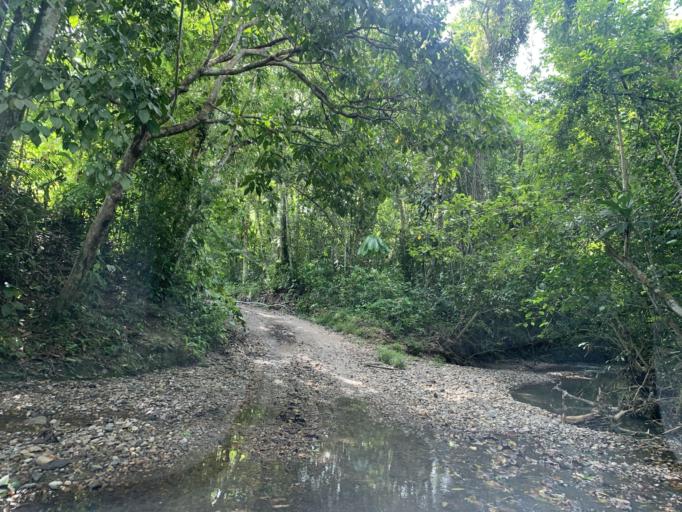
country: CO
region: Boyaca
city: Puerto Boyaca
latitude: 6.0102
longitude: -74.3898
